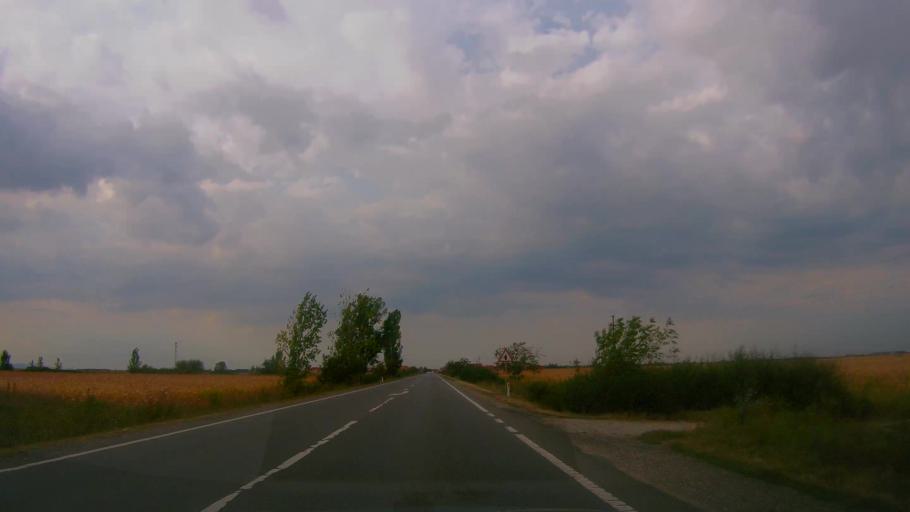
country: RO
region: Satu Mare
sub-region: Comuna Botiz
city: Botiz
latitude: 47.8443
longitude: 22.9651
